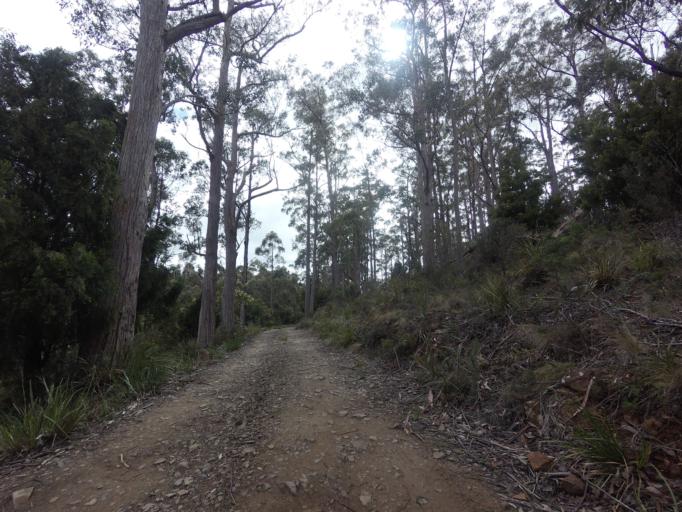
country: AU
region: Tasmania
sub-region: Huon Valley
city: Geeveston
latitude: -43.4567
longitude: 146.9042
